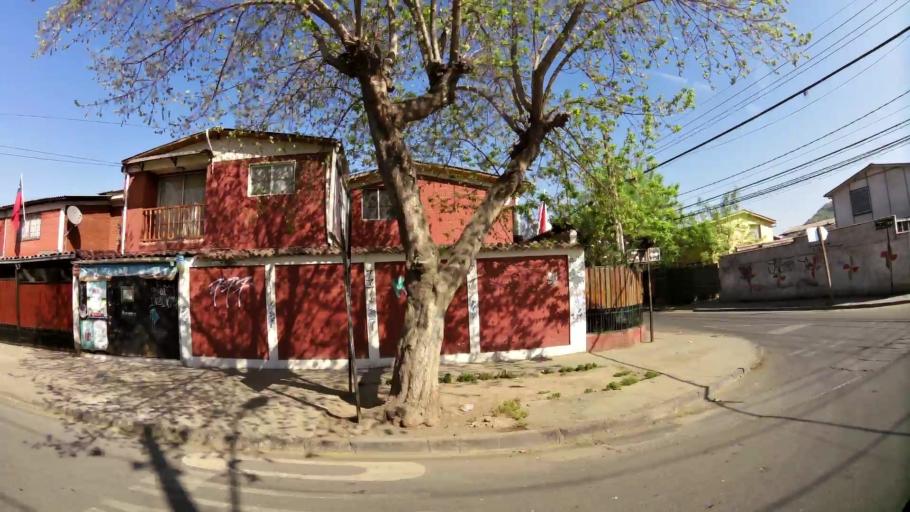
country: CL
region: Santiago Metropolitan
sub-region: Provincia de Chacabuco
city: Chicureo Abajo
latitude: -33.3576
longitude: -70.6866
